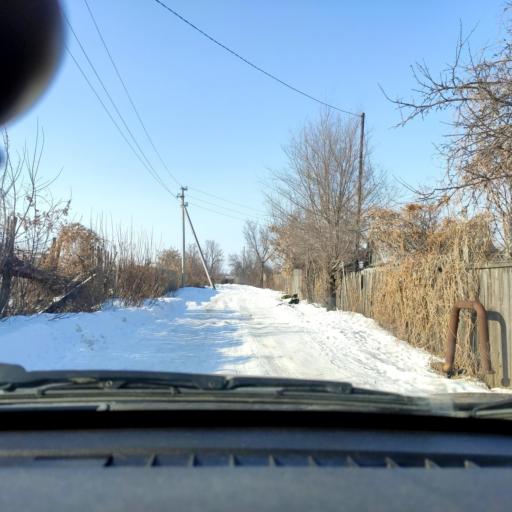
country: RU
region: Samara
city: Tol'yatti
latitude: 53.5707
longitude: 49.4535
